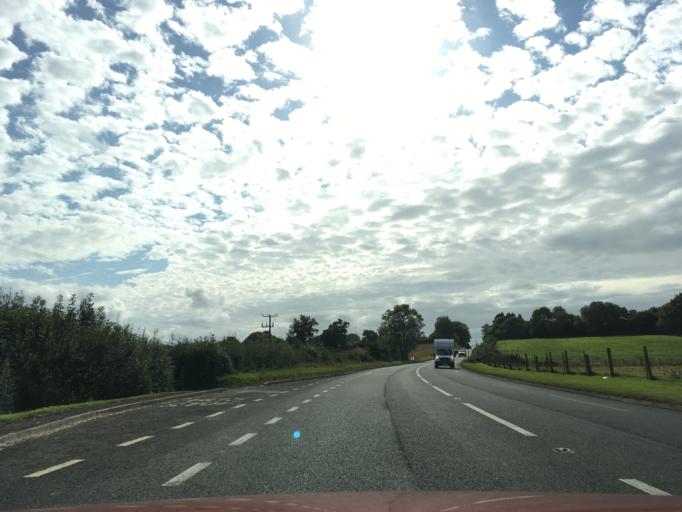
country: GB
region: England
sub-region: Gloucestershire
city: Dursley
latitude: 51.7074
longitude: -2.3896
